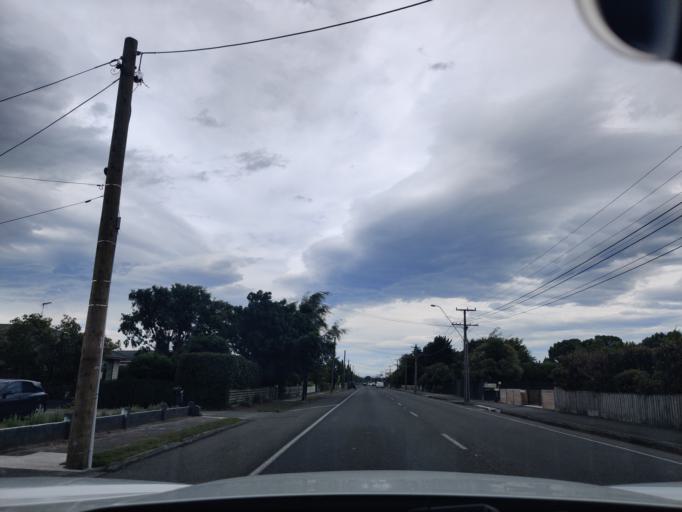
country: NZ
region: Wellington
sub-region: Masterton District
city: Masterton
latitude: -41.0391
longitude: 175.5131
